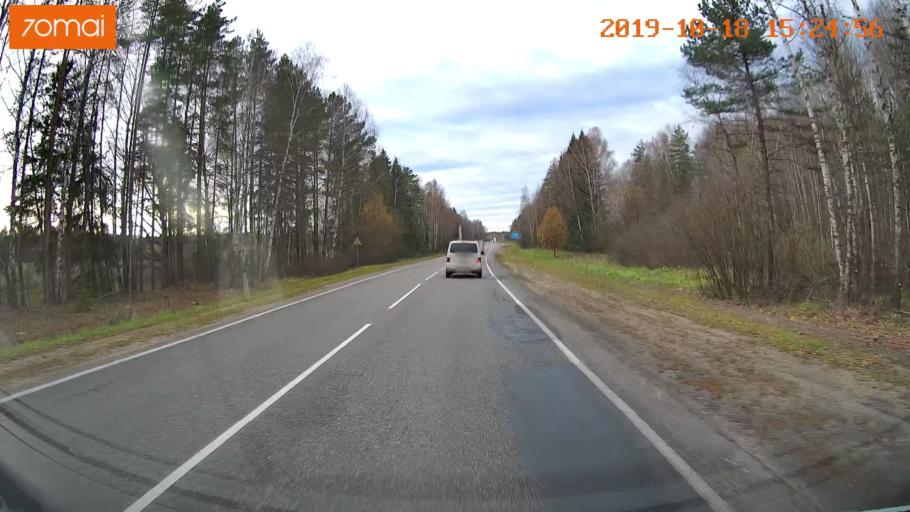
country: RU
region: Vladimir
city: Anopino
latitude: 55.7380
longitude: 40.7148
